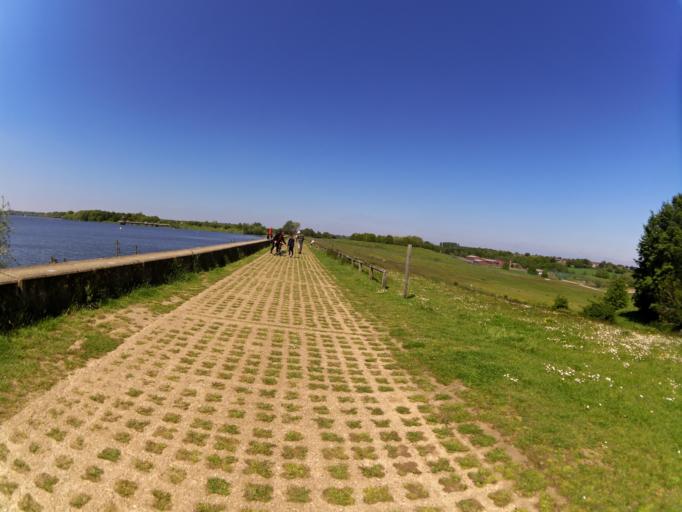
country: GB
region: England
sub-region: Essex
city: Mistley
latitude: 51.9759
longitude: 1.1469
